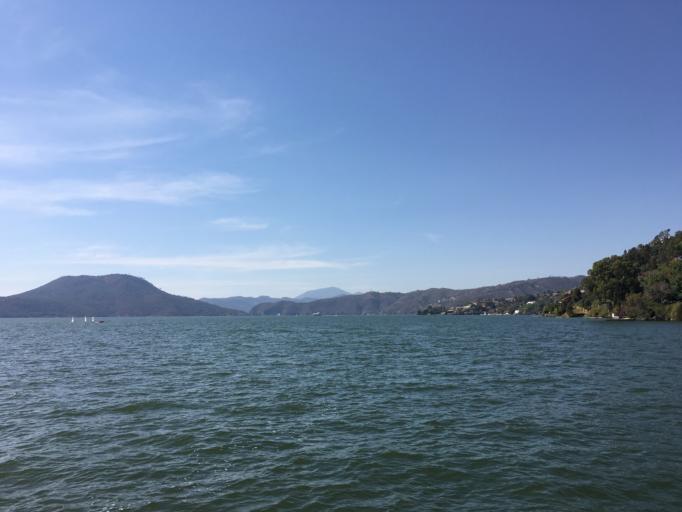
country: MX
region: Mexico
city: Valle de Bravo
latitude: 19.1889
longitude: -100.1349
